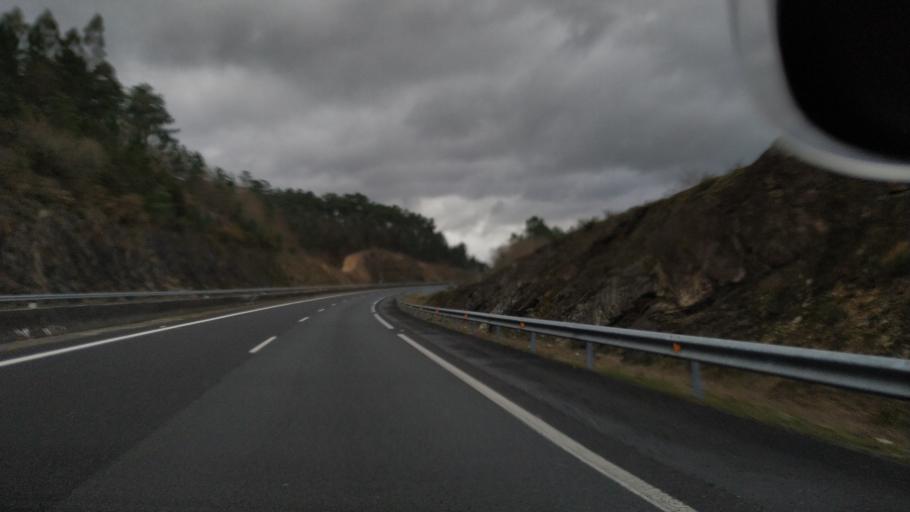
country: ES
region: Galicia
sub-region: Provincia da Coruna
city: Vedra
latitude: 42.7952
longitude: -8.4827
